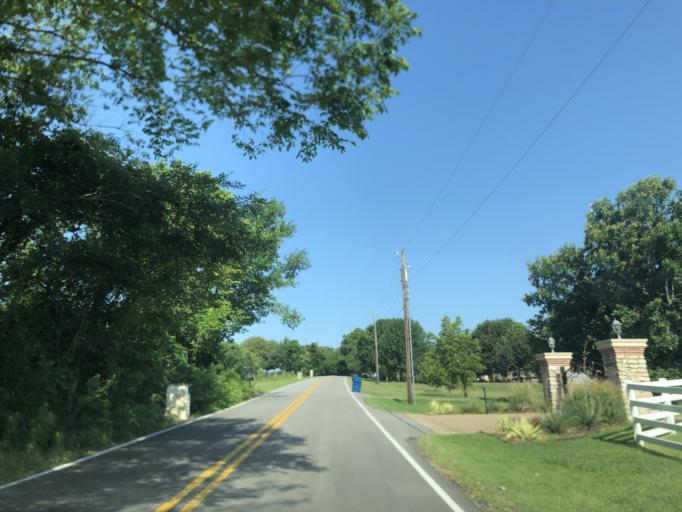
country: US
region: Texas
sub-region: Dallas County
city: Sunnyvale
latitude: 32.8285
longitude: -96.5701
